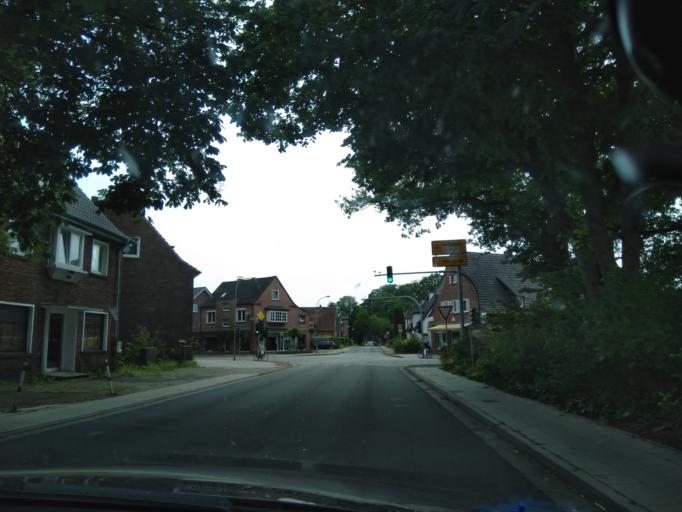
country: DE
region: Lower Saxony
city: Nordhorn
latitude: 52.4518
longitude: 7.0576
